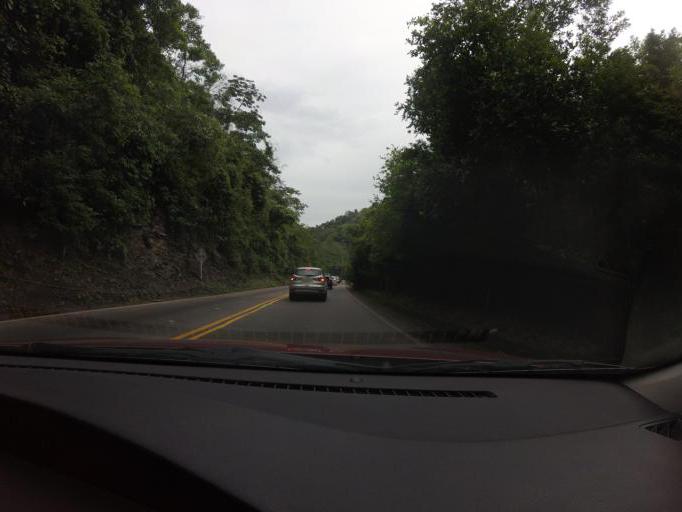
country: CO
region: Cundinamarca
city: Villeta
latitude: 5.0200
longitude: -74.5203
